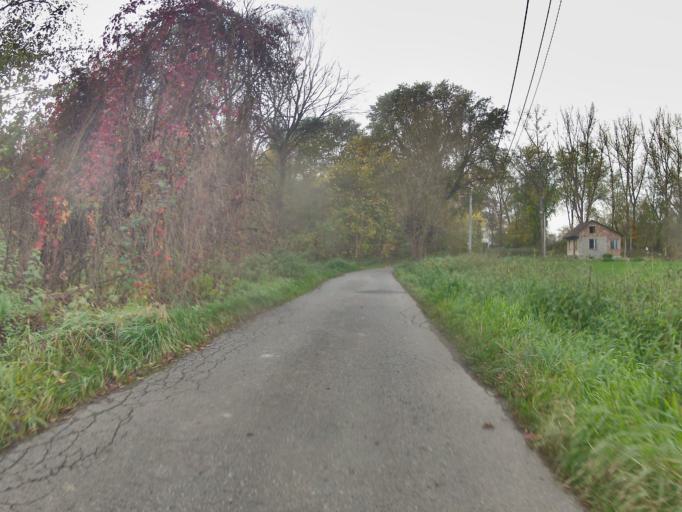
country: PL
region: Lesser Poland Voivodeship
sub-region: Powiat wielicki
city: Wegrzce Wielkie
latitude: 50.0465
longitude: 20.1007
